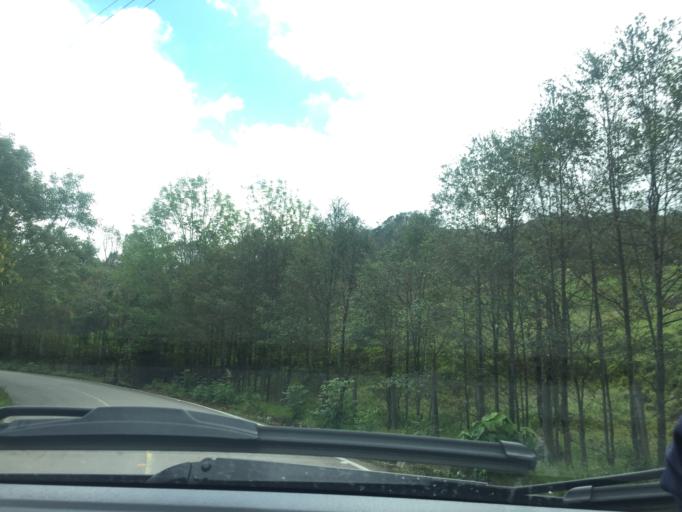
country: CO
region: Cundinamarca
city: Supata
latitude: 5.0424
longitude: -74.2420
